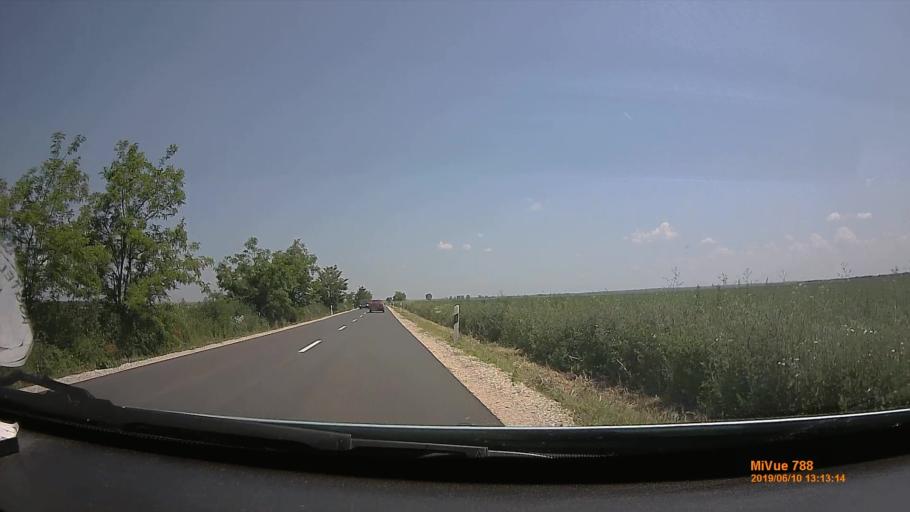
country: HU
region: Borsod-Abauj-Zemplen
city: Hernadnemeti
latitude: 48.0608
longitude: 21.0012
